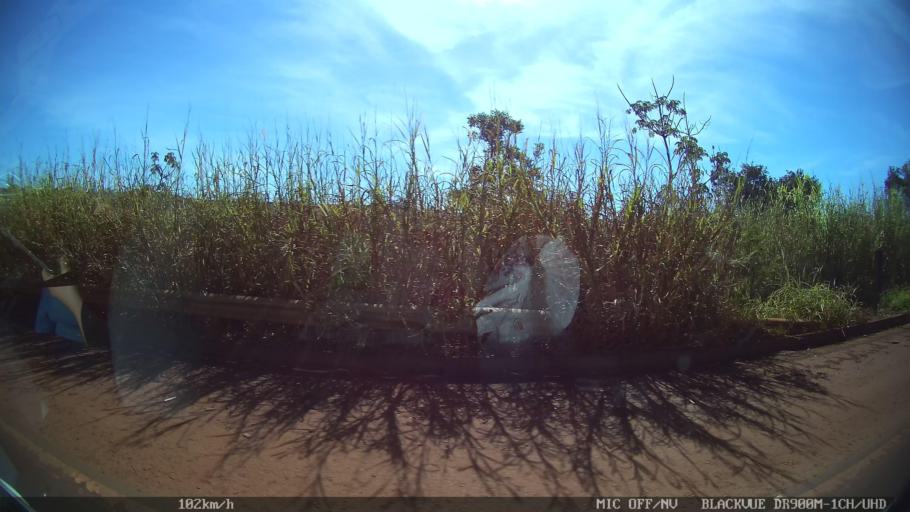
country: BR
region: Sao Paulo
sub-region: Sao Joaquim Da Barra
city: Sao Joaquim da Barra
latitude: -20.5521
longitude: -47.6599
